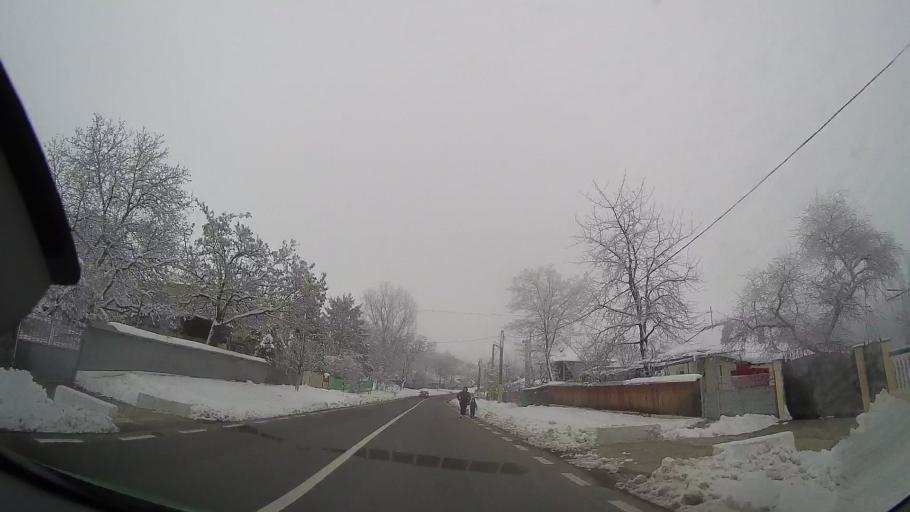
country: RO
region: Neamt
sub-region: Comuna Poenari
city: Poienari
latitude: 46.8864
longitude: 27.1308
